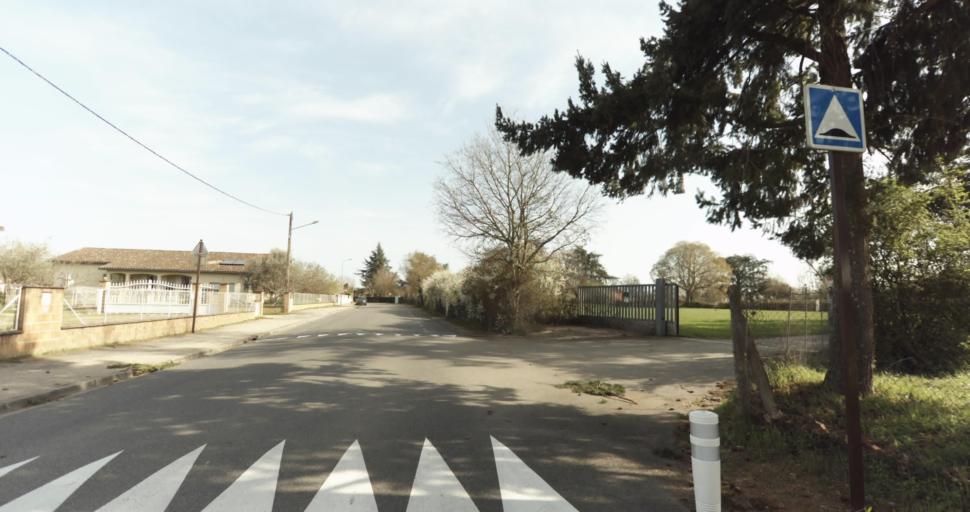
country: FR
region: Midi-Pyrenees
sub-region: Departement du Tarn
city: Saint-Sulpice-la-Pointe
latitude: 43.7780
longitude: 1.6807
